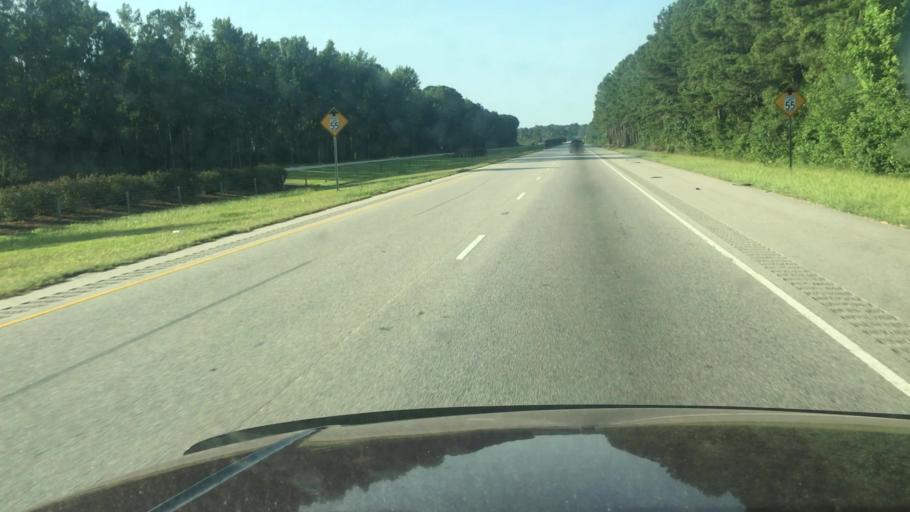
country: US
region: North Carolina
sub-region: Cumberland County
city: Fayetteville
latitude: 34.9915
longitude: -78.8621
